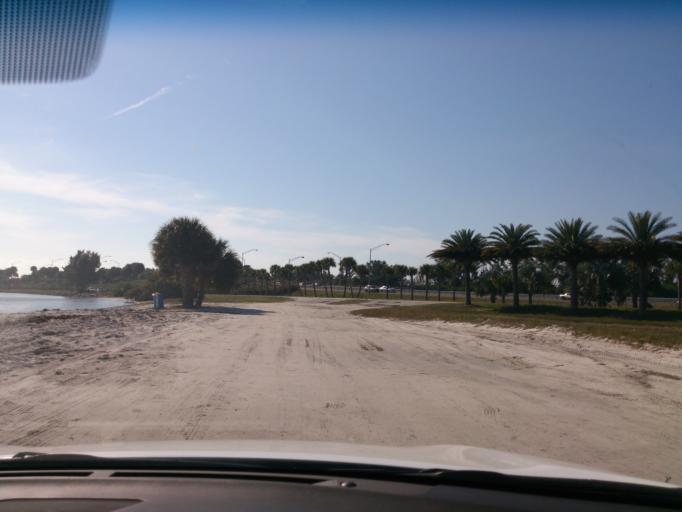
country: US
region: Florida
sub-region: Pinellas County
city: Tierra Verde
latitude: 27.6539
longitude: -82.6756
